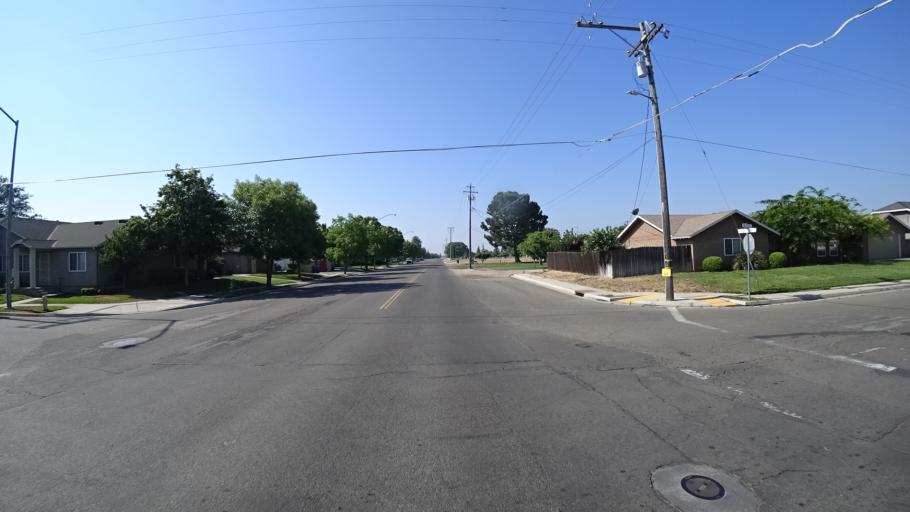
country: US
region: California
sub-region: Fresno County
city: Kingsburg
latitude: 36.5071
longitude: -119.5568
